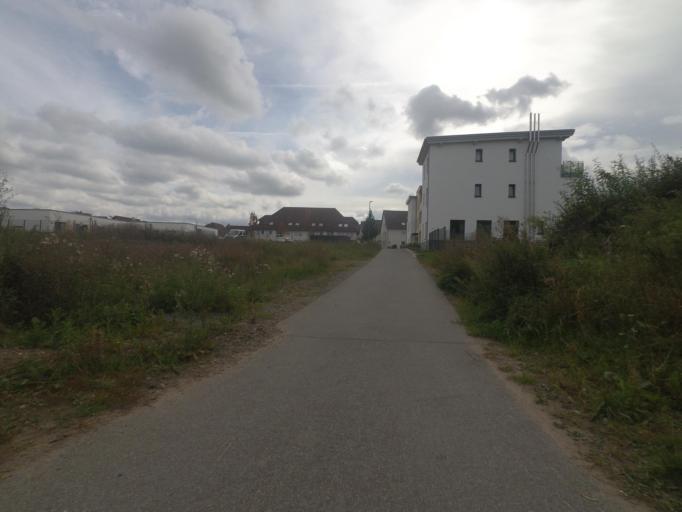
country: DE
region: North Rhine-Westphalia
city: Iserlohn
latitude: 51.4238
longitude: 7.6683
